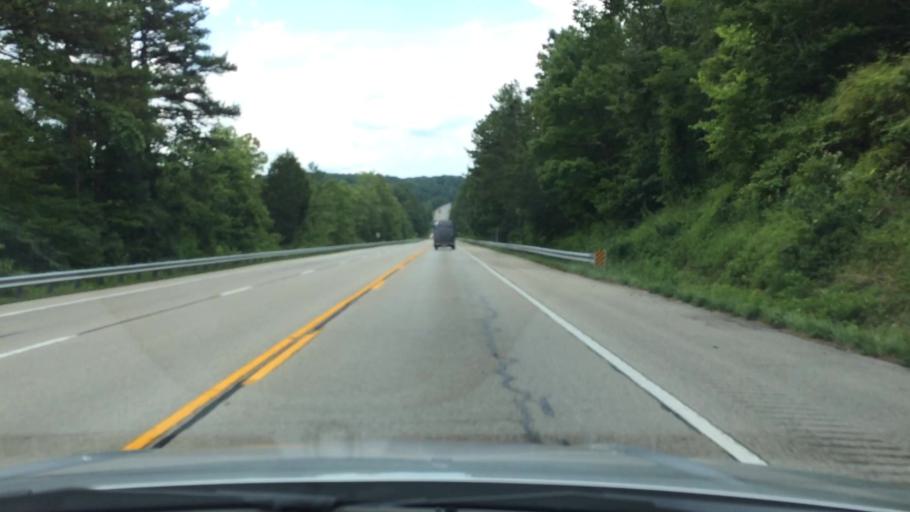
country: US
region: Kentucky
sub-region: McCreary County
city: Whitley City
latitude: 36.9081
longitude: -84.5082
